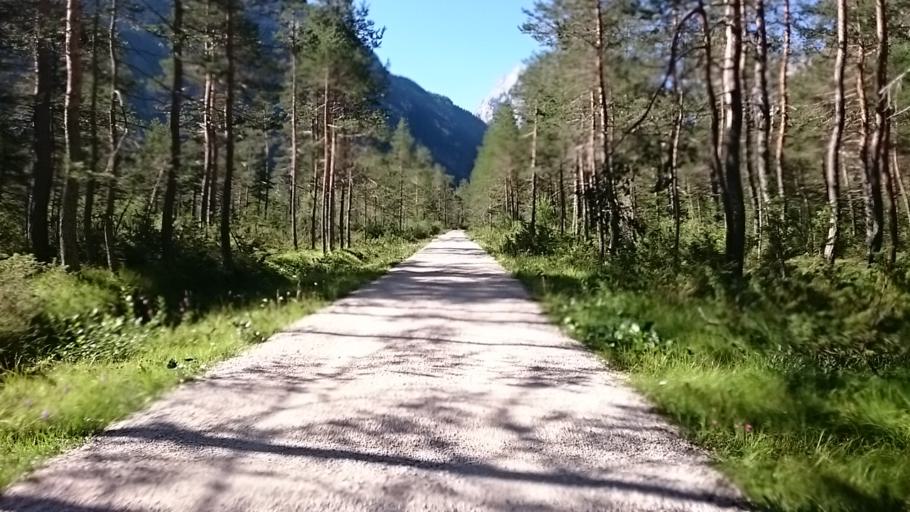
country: IT
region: Trentino-Alto Adige
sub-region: Bolzano
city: Dobbiaco
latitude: 46.6369
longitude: 12.2320
